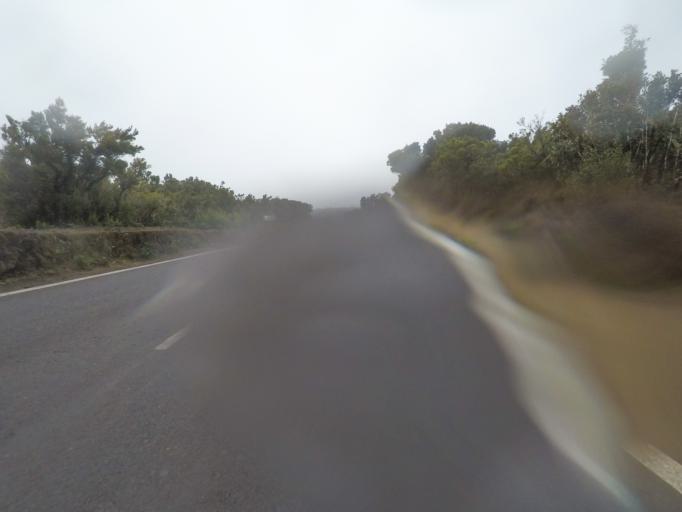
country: ES
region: Canary Islands
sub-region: Provincia de Santa Cruz de Tenerife
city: Vallehermosa
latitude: 28.1502
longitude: -17.3075
